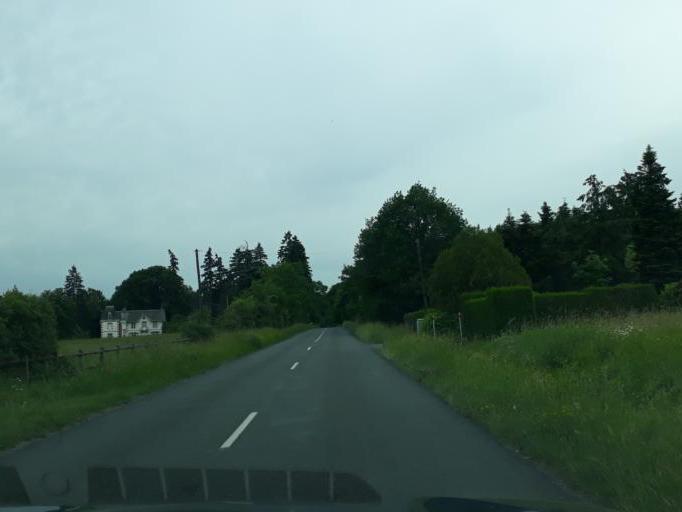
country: FR
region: Centre
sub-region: Departement du Loiret
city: Saint-Pere-sur-Loire
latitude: 47.7483
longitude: 2.3570
